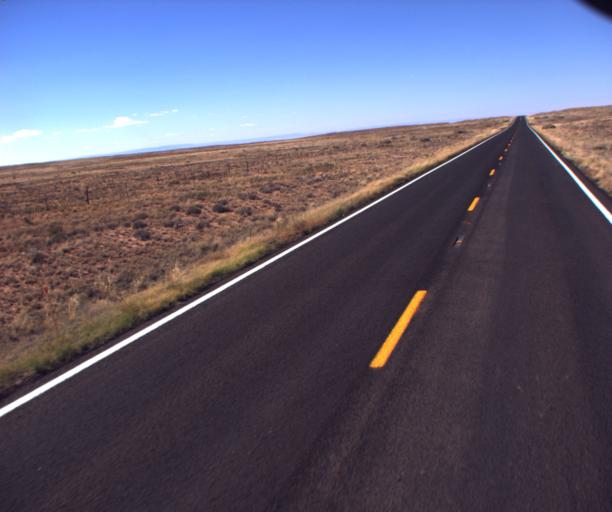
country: US
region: Arizona
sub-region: Coconino County
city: Tuba City
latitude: 35.9670
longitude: -110.9541
